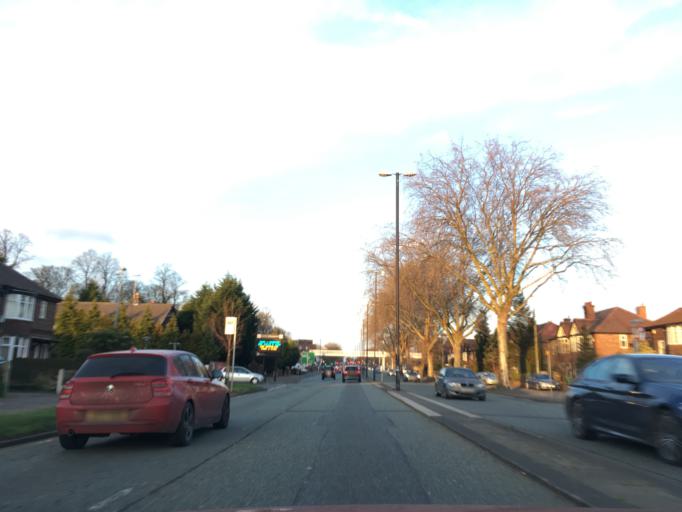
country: GB
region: England
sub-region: Manchester
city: Didsbury
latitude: 53.4065
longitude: -2.2220
